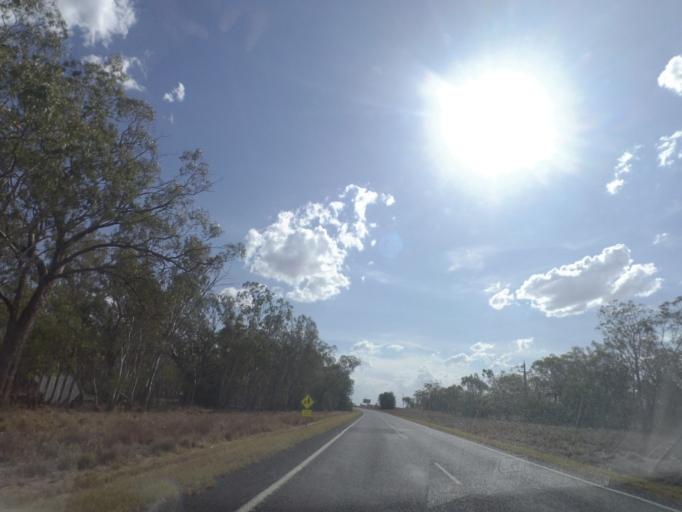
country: AU
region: New South Wales
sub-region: Moree Plains
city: Boggabilla
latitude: -28.5478
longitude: 150.8726
